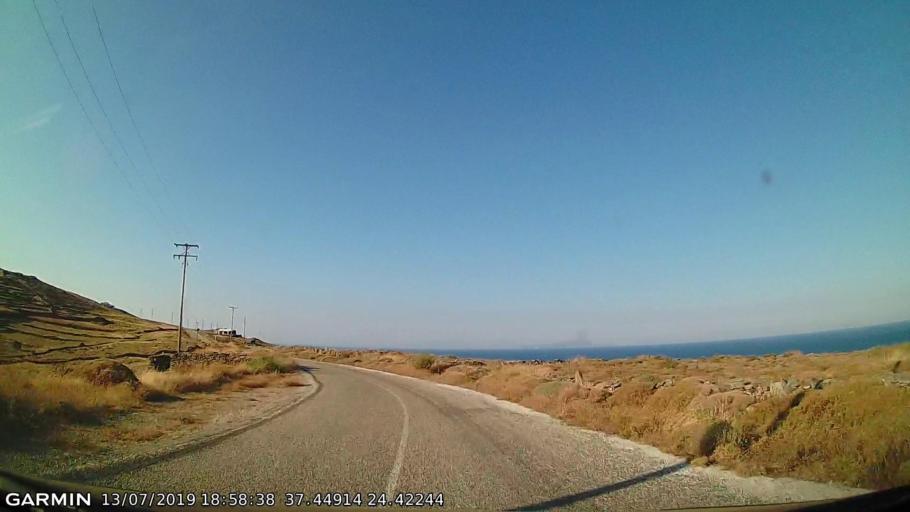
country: GR
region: South Aegean
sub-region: Nomos Kykladon
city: Kythnos
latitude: 37.4495
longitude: 24.4230
